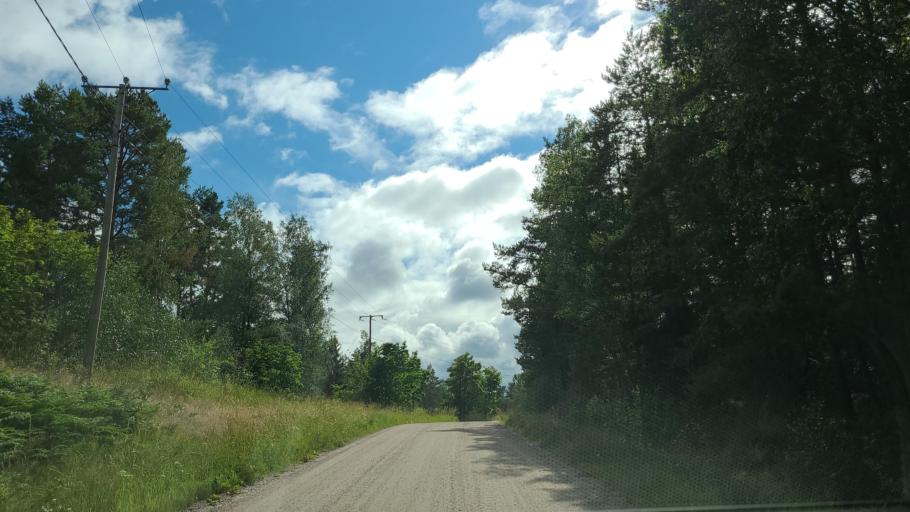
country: FI
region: Varsinais-Suomi
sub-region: Aboland-Turunmaa
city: Nagu
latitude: 60.1968
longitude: 21.7757
